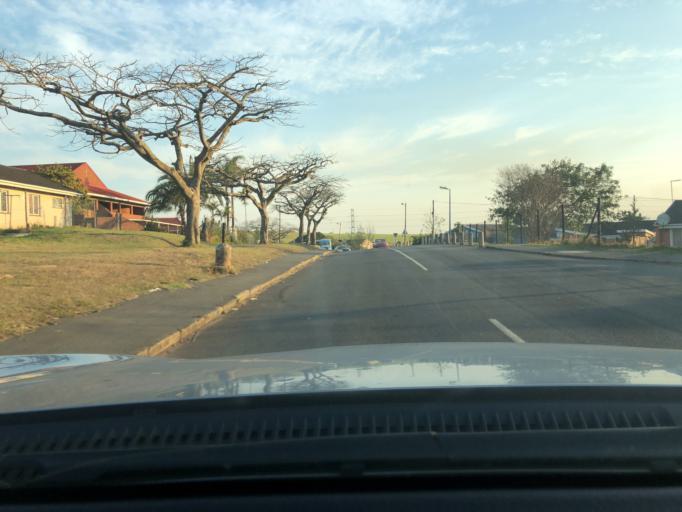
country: ZA
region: KwaZulu-Natal
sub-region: iLembe District Municipality
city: Ballitoville
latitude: -29.5825
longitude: 31.0984
